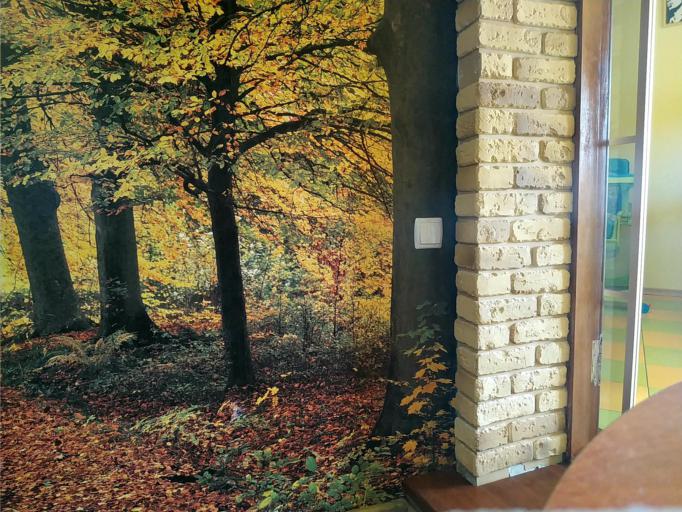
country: RU
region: Smolensk
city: Katyn'
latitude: 54.9419
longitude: 31.7225
